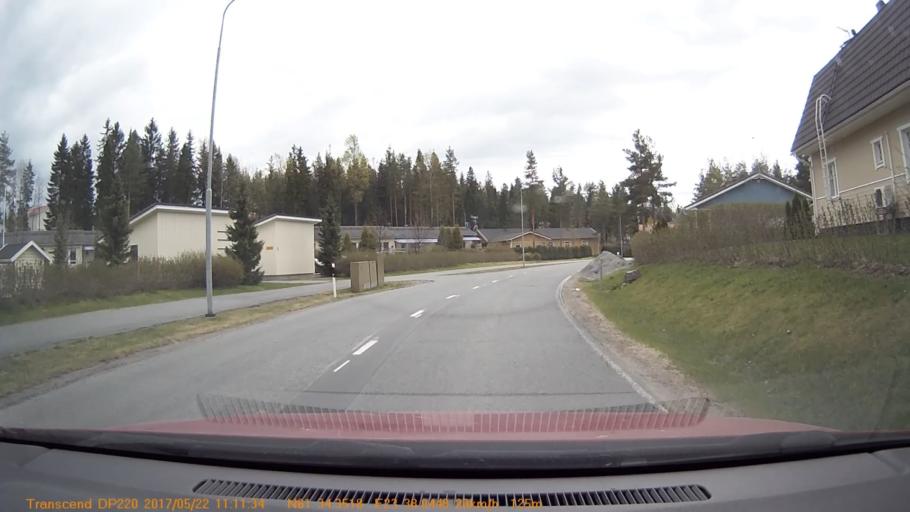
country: FI
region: Pirkanmaa
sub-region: Tampere
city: Yloejaervi
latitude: 61.5725
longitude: 23.6341
